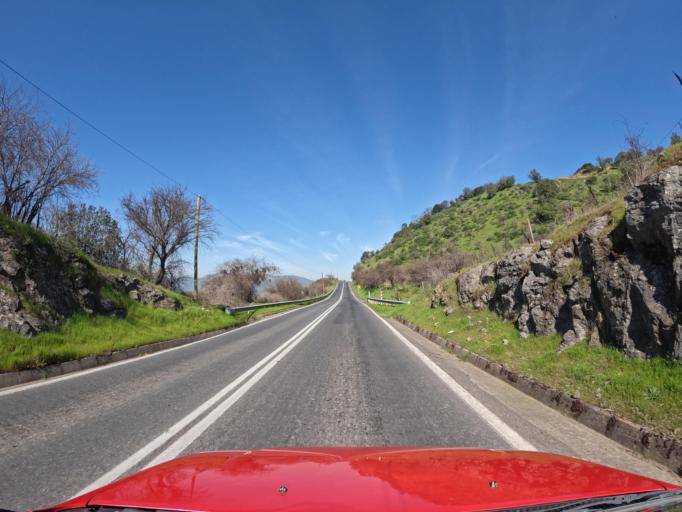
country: CL
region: Maule
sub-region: Provincia de Curico
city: Rauco
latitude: -34.9737
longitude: -71.3822
